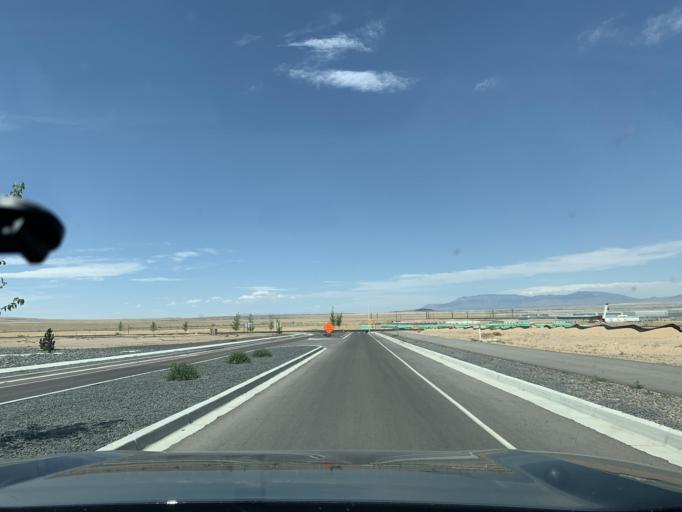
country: US
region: New Mexico
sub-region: Valencia County
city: Los Lunas
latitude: 34.8197
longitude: -106.7971
